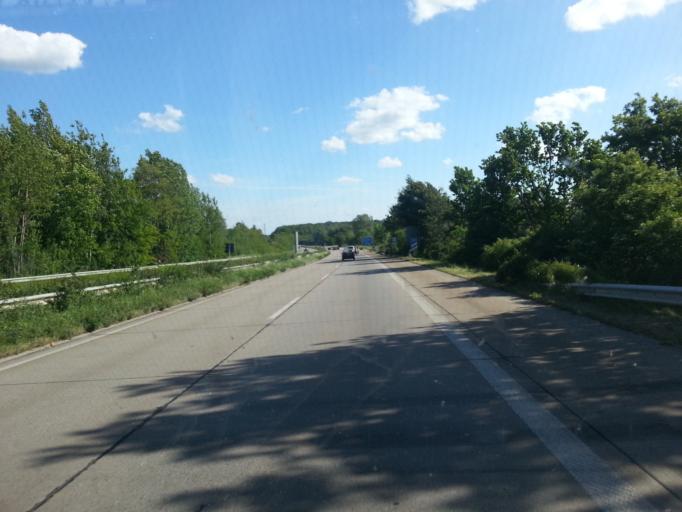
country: DE
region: Schleswig-Holstein
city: Scharbeutz
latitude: 54.0416
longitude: 10.7282
